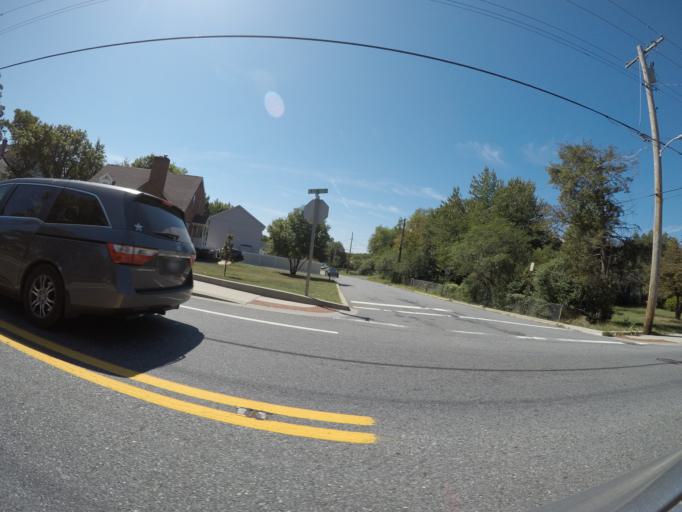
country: US
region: Maryland
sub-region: Harford County
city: Aberdeen
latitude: 39.5154
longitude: -76.1780
